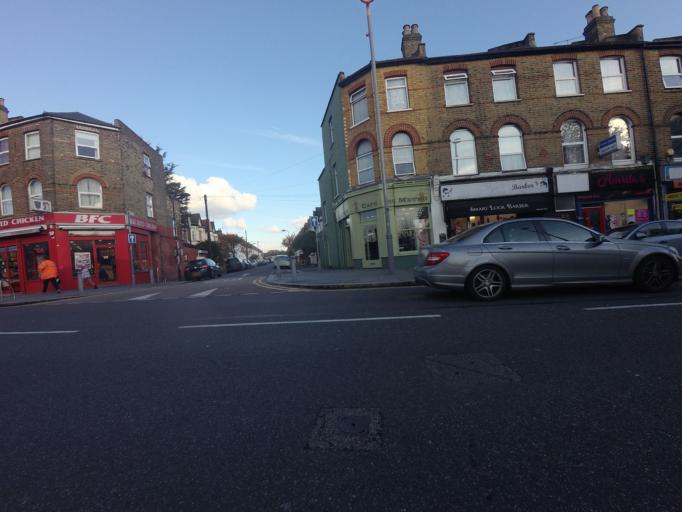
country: GB
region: England
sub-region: Greater London
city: Walthamstow
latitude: 51.5547
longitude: -0.0053
